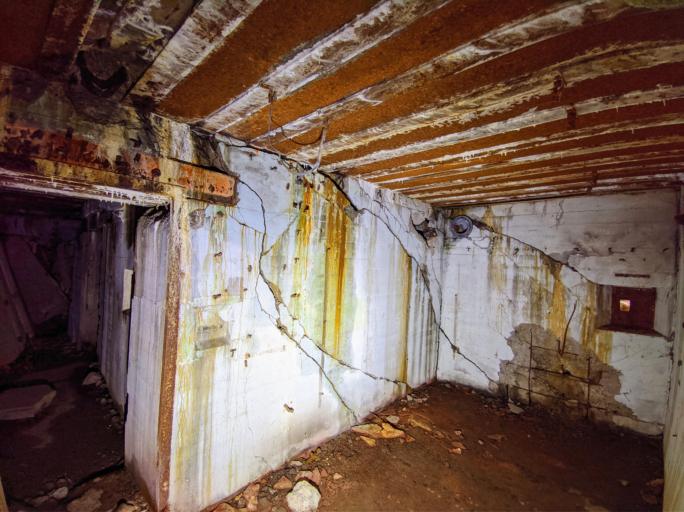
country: PL
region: Lubusz
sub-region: Powiat miedzyrzecki
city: Bledzew
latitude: 52.4464
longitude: 15.4554
